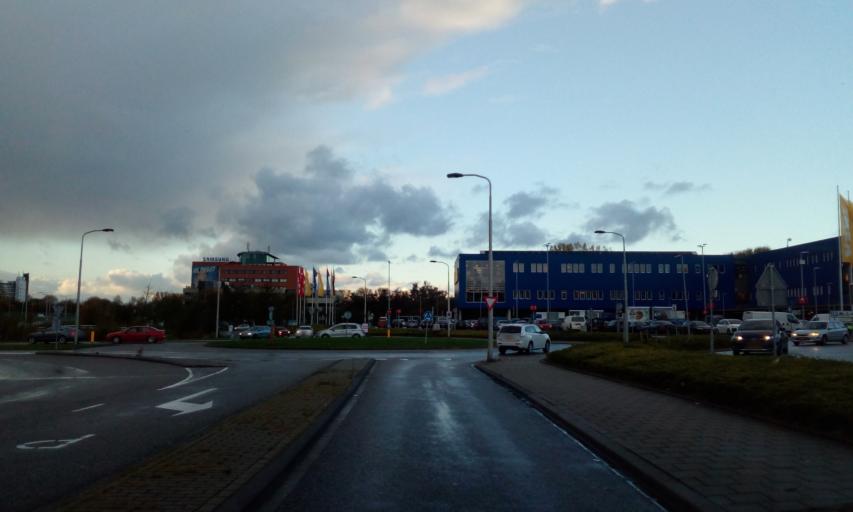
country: NL
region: South Holland
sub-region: Gemeente Delft
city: Delft
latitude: 52.0119
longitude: 4.3805
